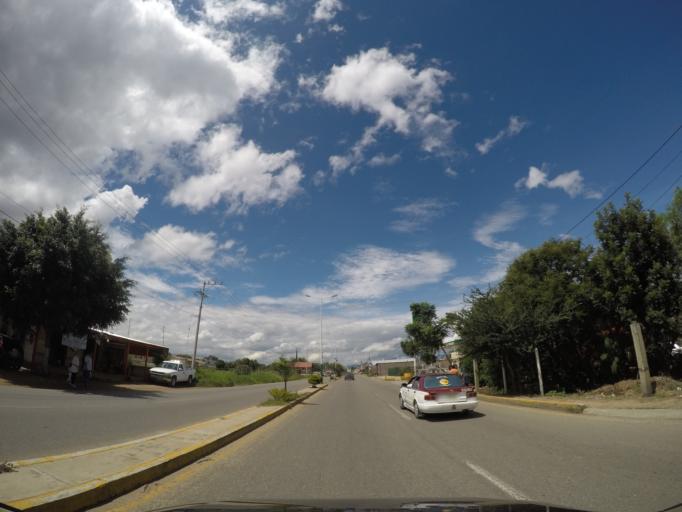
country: MX
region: Oaxaca
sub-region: Santa Cruz Xoxocotlan
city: Santa Cruz Xoxocotlan
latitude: 17.0199
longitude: -96.7315
